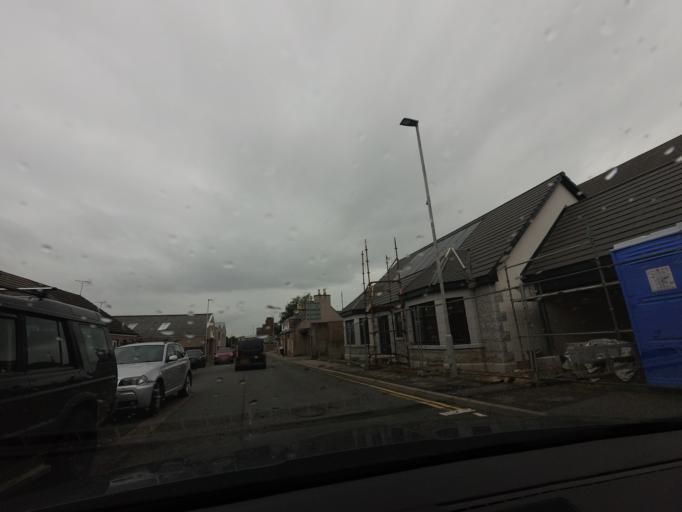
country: GB
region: Scotland
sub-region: Aberdeenshire
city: Turriff
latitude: 57.5390
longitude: -2.4616
